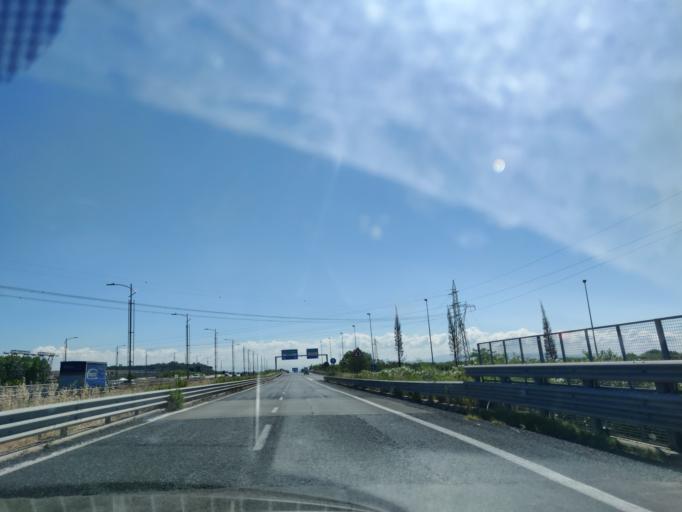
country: IT
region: Latium
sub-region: Citta metropolitana di Roma Capitale
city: Ponte Galeria-La Pisana
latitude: 41.8133
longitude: 12.3386
